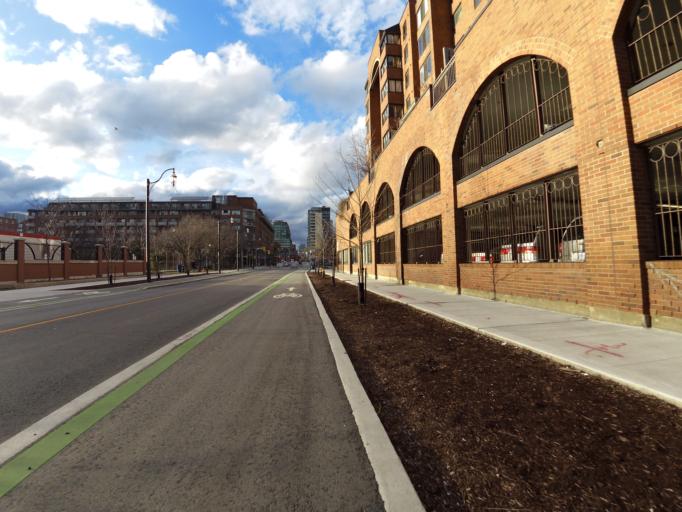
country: CA
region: Ontario
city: Toronto
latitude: 43.6481
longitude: -79.3668
